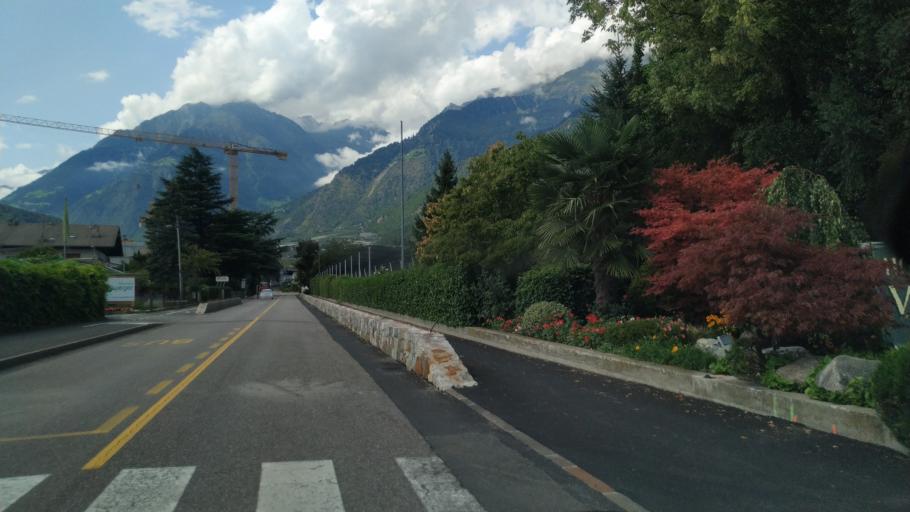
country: IT
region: Trentino-Alto Adige
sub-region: Bolzano
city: Lagundo
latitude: 46.6792
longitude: 11.1381
